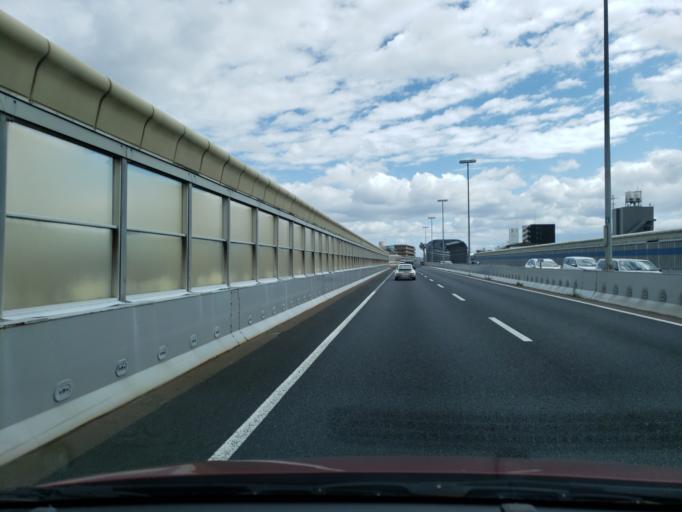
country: JP
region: Hyogo
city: Nishinomiya-hama
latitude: 34.7338
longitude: 135.3408
